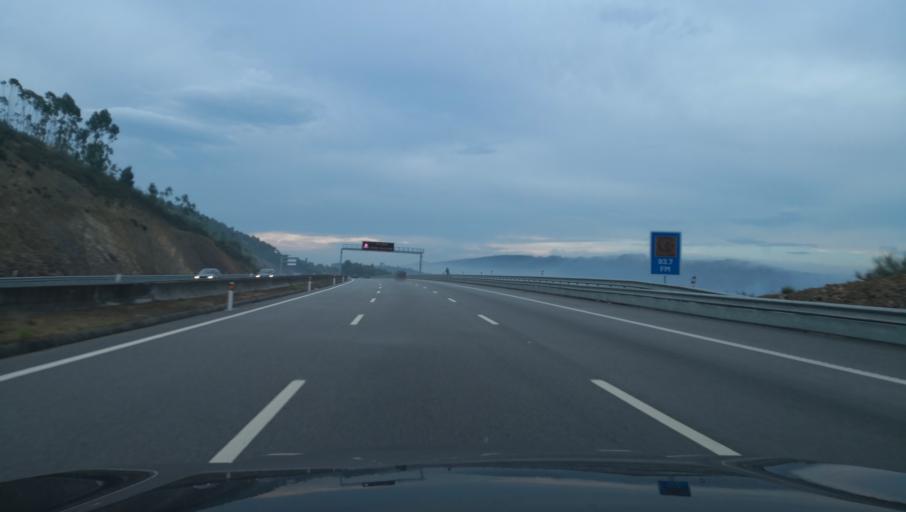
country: PT
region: Porto
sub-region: Paredes
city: Recarei
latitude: 41.1196
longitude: -8.4335
